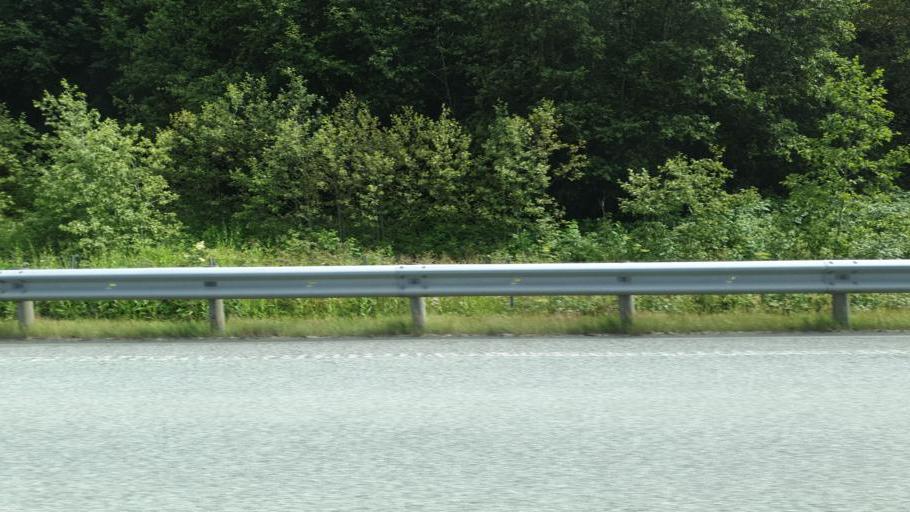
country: NO
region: Sor-Trondelag
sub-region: Midtre Gauldal
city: Storen
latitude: 63.0577
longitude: 10.2914
